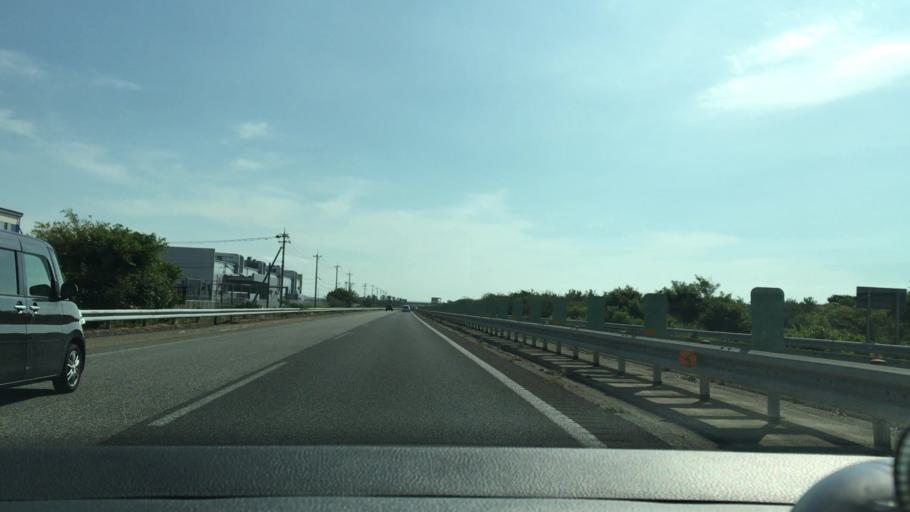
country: JP
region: Ishikawa
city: Komatsu
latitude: 36.3825
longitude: 136.3735
